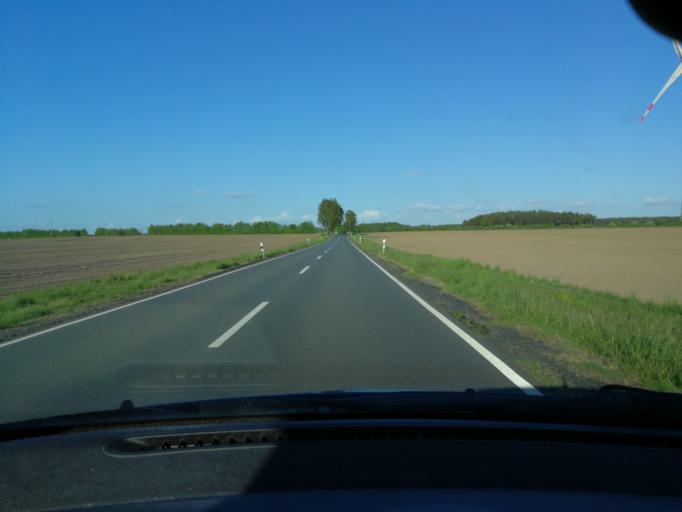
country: DE
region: Lower Saxony
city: Betzendorf
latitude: 53.1033
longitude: 10.2811
